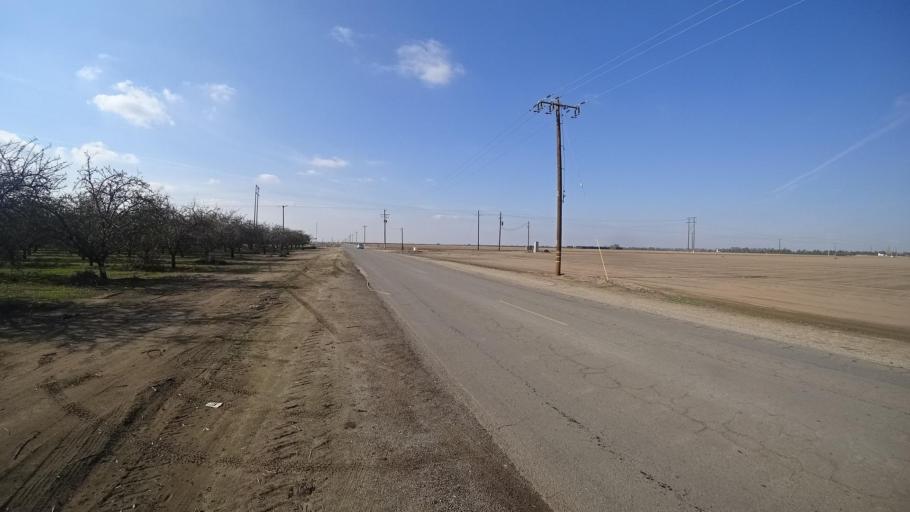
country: US
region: California
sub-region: Kern County
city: Arvin
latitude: 35.2674
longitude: -118.8059
